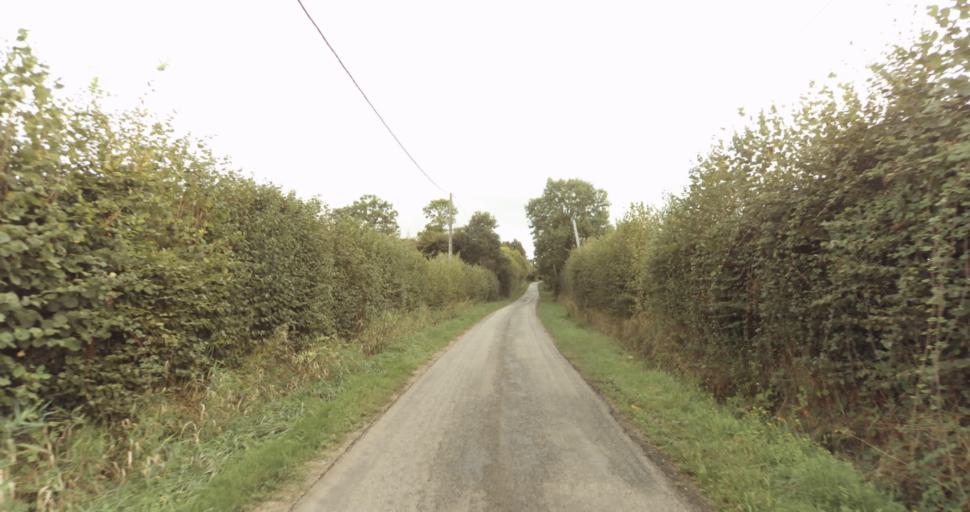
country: FR
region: Lower Normandy
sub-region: Departement de l'Orne
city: Sainte-Gauburge-Sainte-Colombe
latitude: 48.7043
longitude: 0.3368
